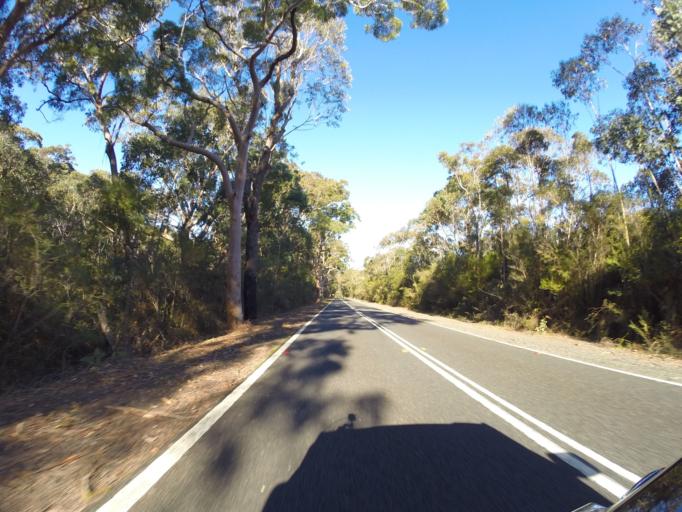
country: AU
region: New South Wales
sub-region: Wollongong
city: Helensburgh
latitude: -34.1475
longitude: 151.0102
